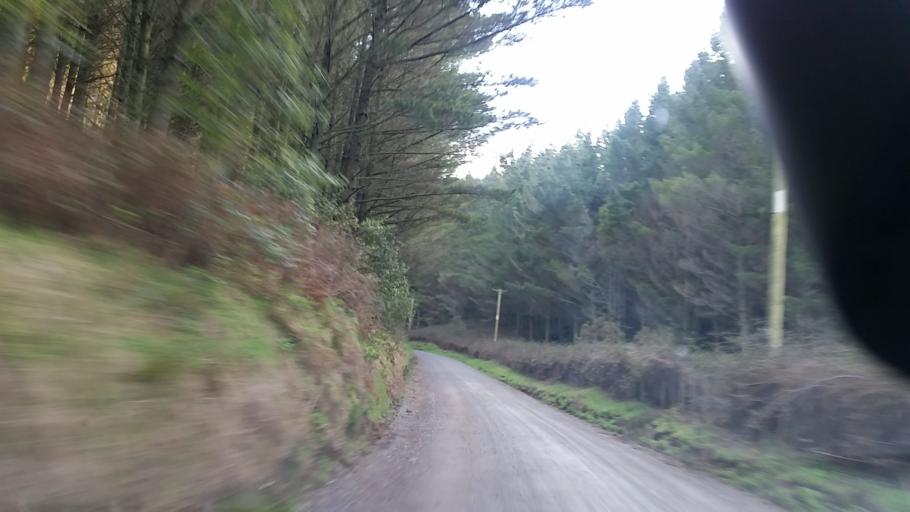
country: NZ
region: Bay of Plenty
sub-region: Rotorua District
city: Rotorua
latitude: -38.2229
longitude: 176.1613
